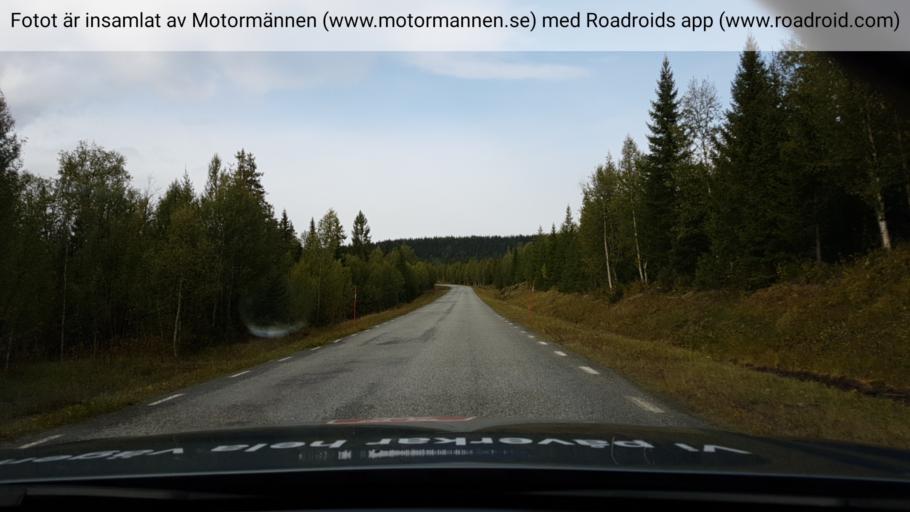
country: SE
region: Jaemtland
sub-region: Are Kommun
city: Are
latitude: 63.7355
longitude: 13.0557
